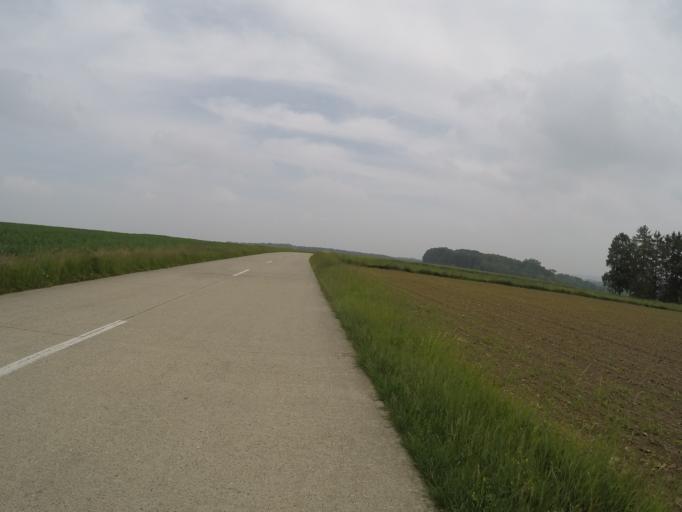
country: BE
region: Wallonia
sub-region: Province de Namur
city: Assesse
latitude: 50.3391
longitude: 4.9966
